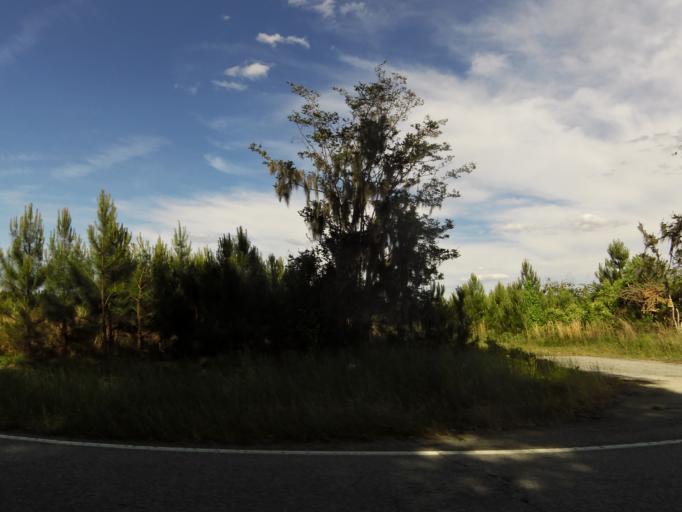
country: US
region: South Carolina
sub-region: Allendale County
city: Allendale
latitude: 33.1365
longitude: -81.1877
